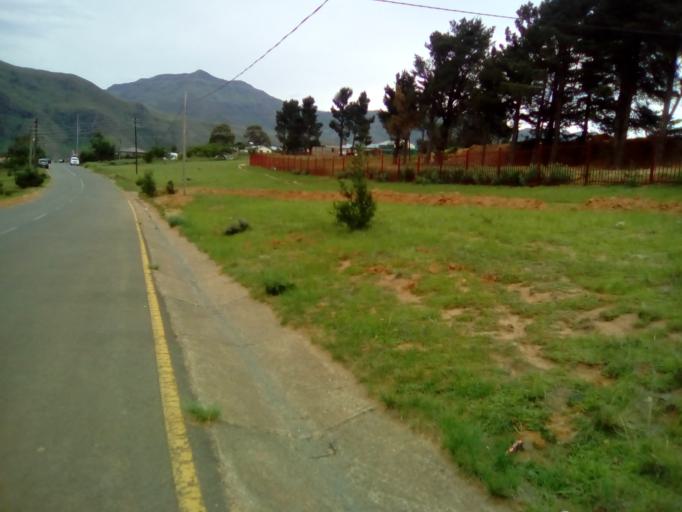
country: LS
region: Qacha's Nek
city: Qacha's Nek
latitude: -30.1103
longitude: 28.6815
